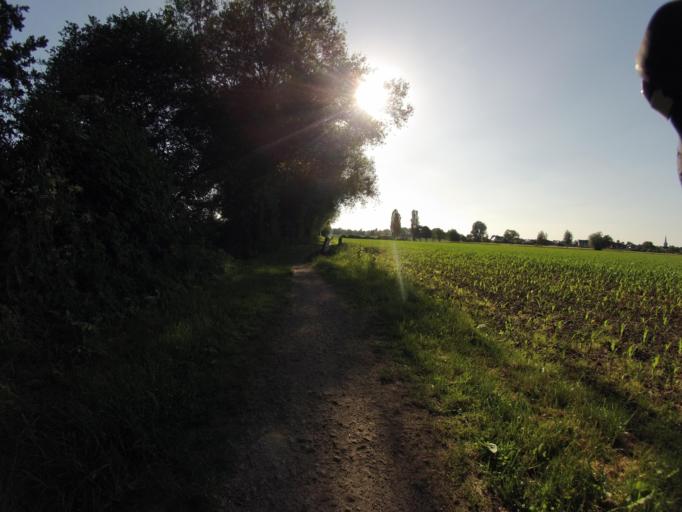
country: DE
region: Lower Saxony
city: Suddendorf
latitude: 52.3088
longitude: 7.2361
